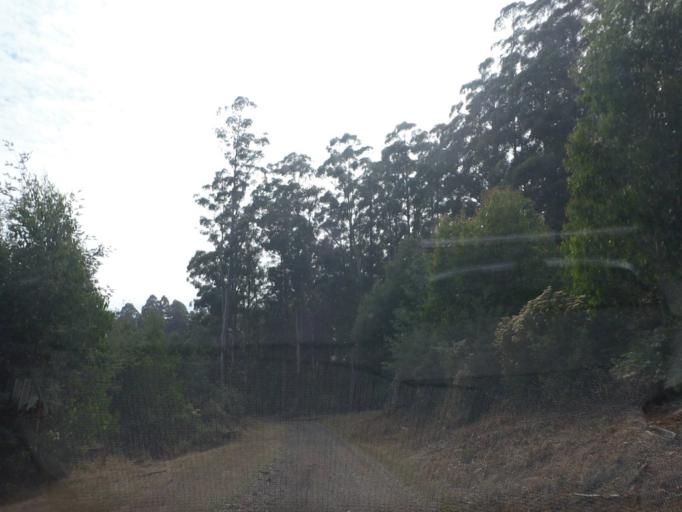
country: AU
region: Victoria
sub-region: Yarra Ranges
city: Healesville
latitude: -37.5846
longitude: 145.5730
